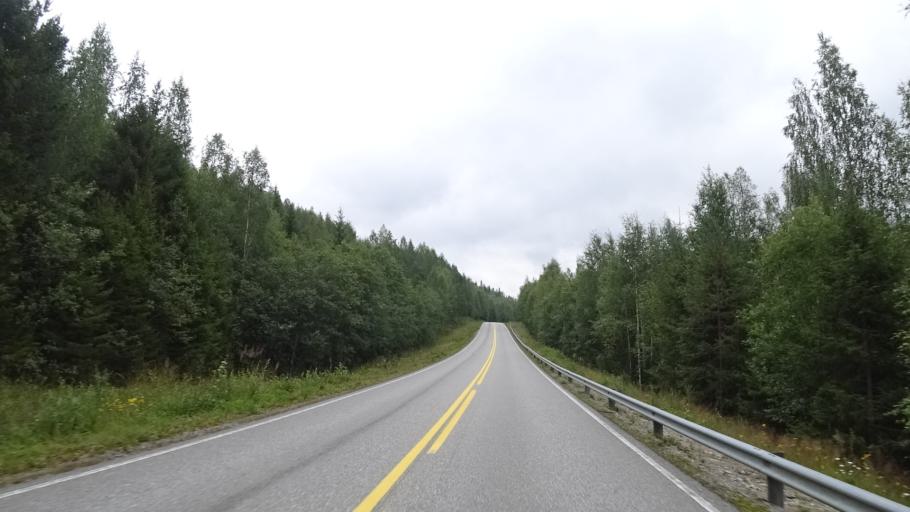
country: FI
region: North Karelia
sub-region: Pielisen Karjala
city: Lieksa
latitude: 63.2807
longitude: 30.5786
